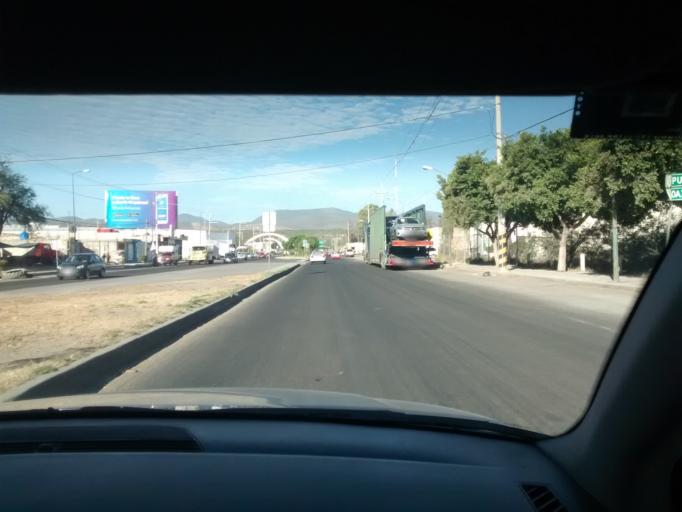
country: MX
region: Puebla
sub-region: Santiago Miahuatlan
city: San Jose Monte Chiquito
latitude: 18.4774
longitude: -97.4238
